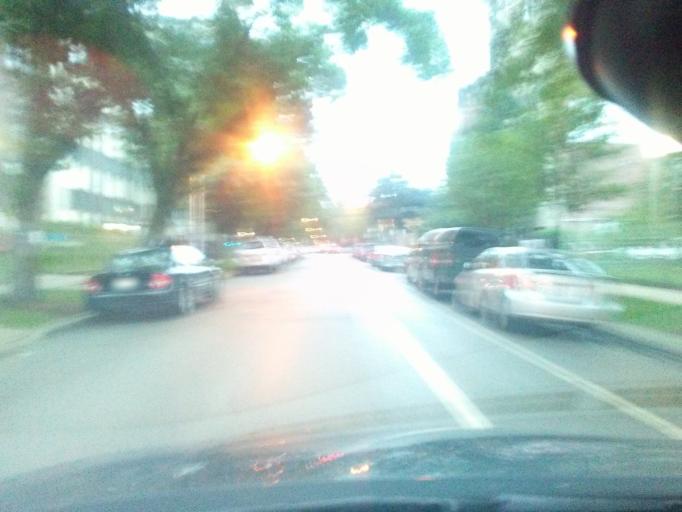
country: US
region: Illinois
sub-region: Cook County
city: Evanston
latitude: 41.9956
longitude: -87.6584
